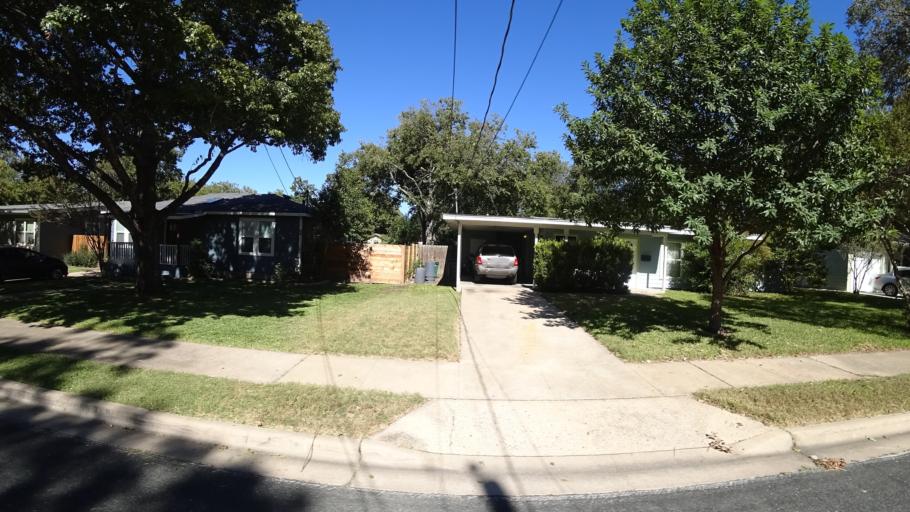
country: US
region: Texas
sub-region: Travis County
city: Austin
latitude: 30.3358
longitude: -97.7314
